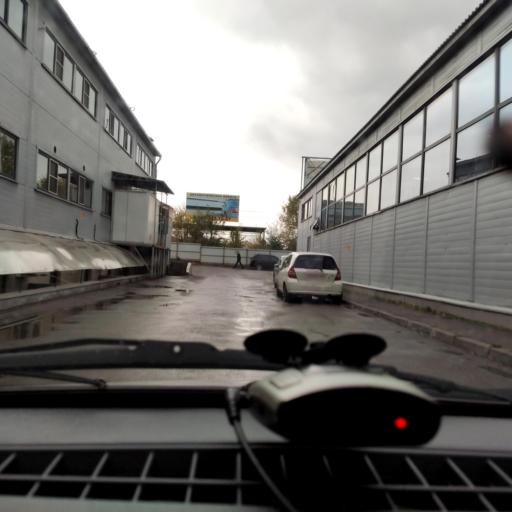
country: RU
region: Voronezj
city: Voronezh
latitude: 51.6690
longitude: 39.1295
